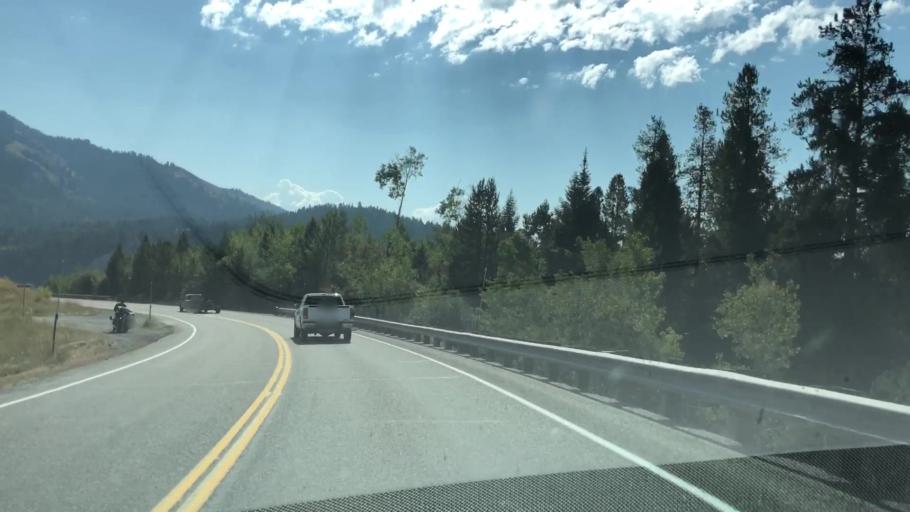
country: US
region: Wyoming
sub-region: Teton County
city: Hoback
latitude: 43.2510
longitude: -111.1162
